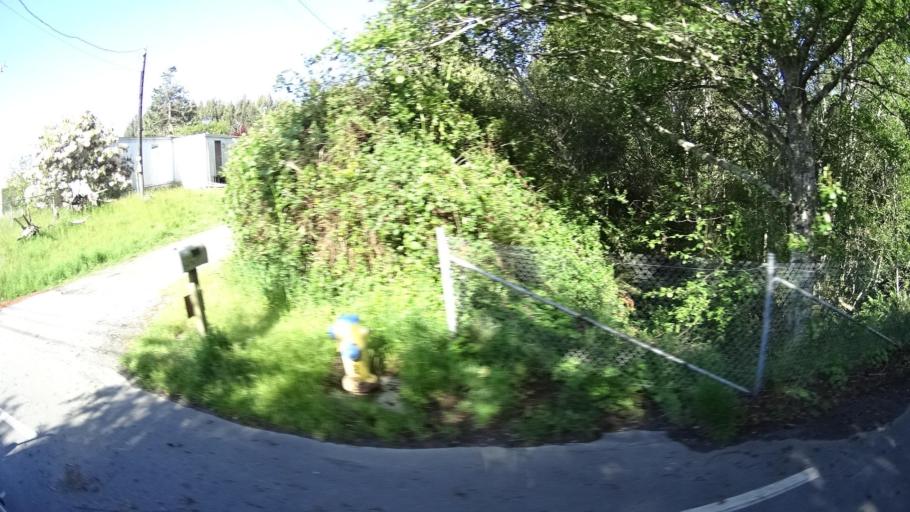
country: US
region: California
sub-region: Humboldt County
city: McKinleyville
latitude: 40.9586
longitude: -124.1104
